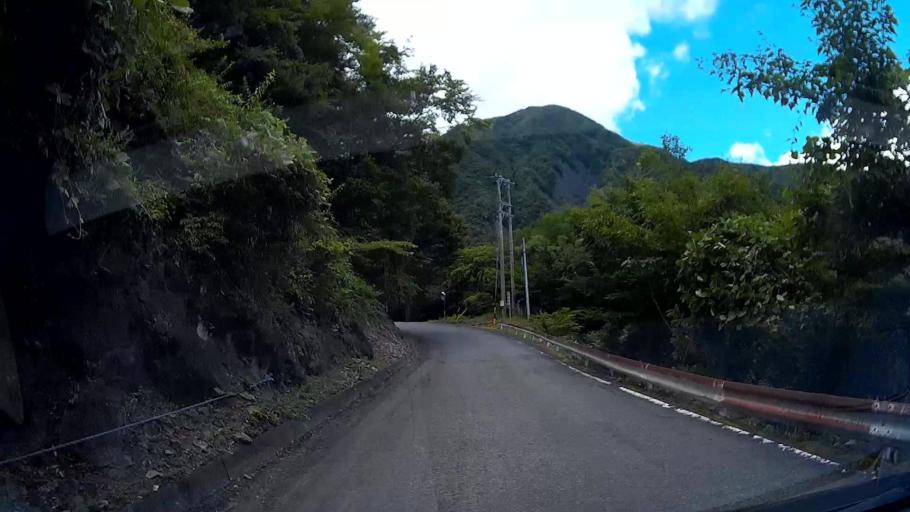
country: JP
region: Shizuoka
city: Shizuoka-shi
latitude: 35.3109
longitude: 138.1874
